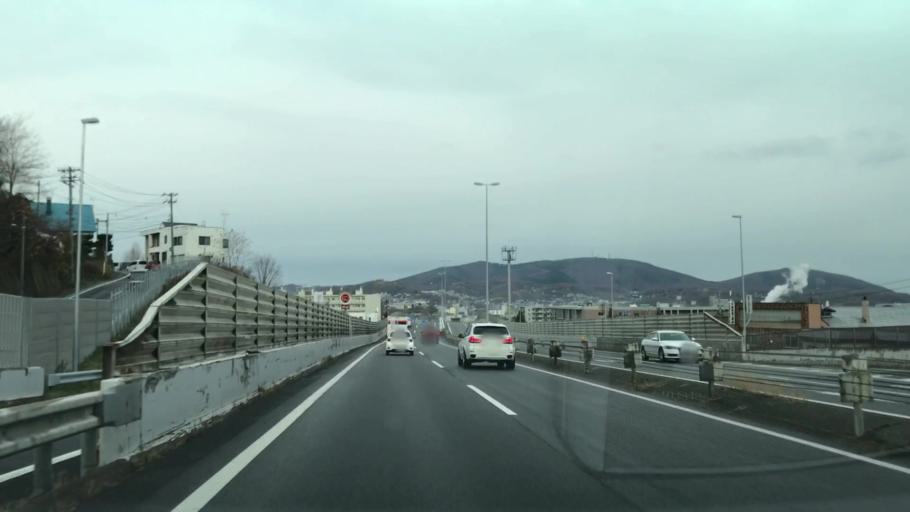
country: JP
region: Hokkaido
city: Otaru
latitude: 43.1800
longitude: 141.0215
